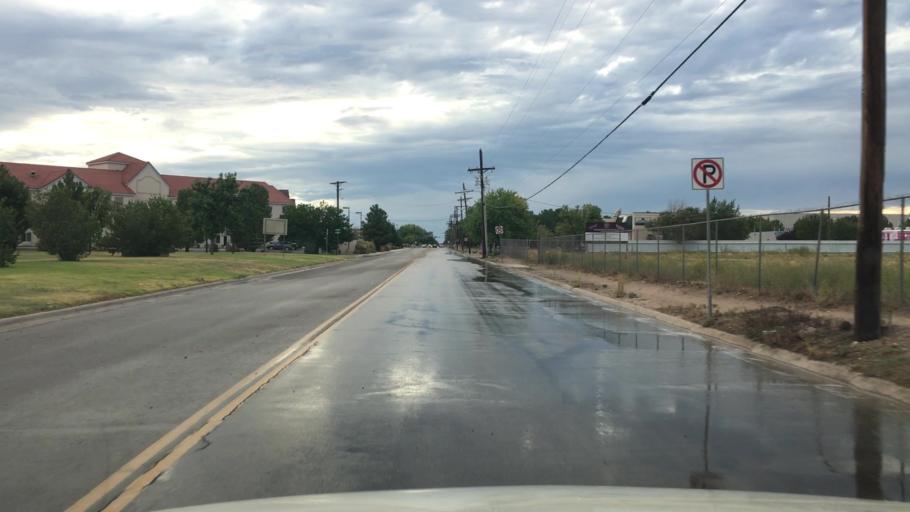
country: US
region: New Mexico
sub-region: Chaves County
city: Roswell
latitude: 33.4160
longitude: -104.5177
